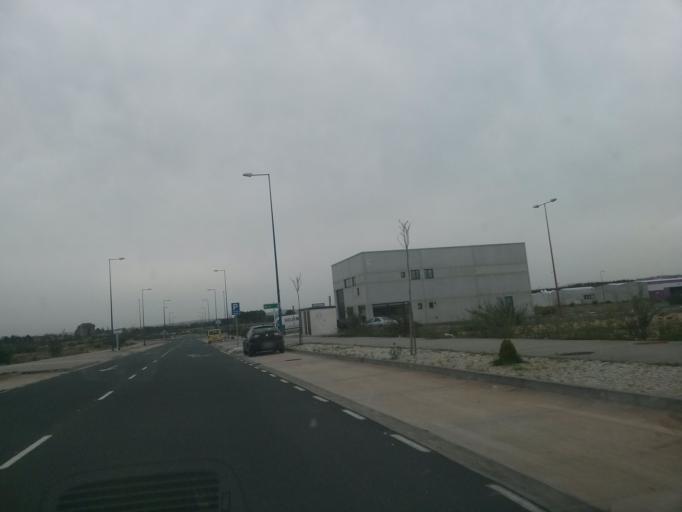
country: ES
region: Galicia
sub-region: Provincia de Lugo
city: Lugo
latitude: 43.0413
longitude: -7.5498
